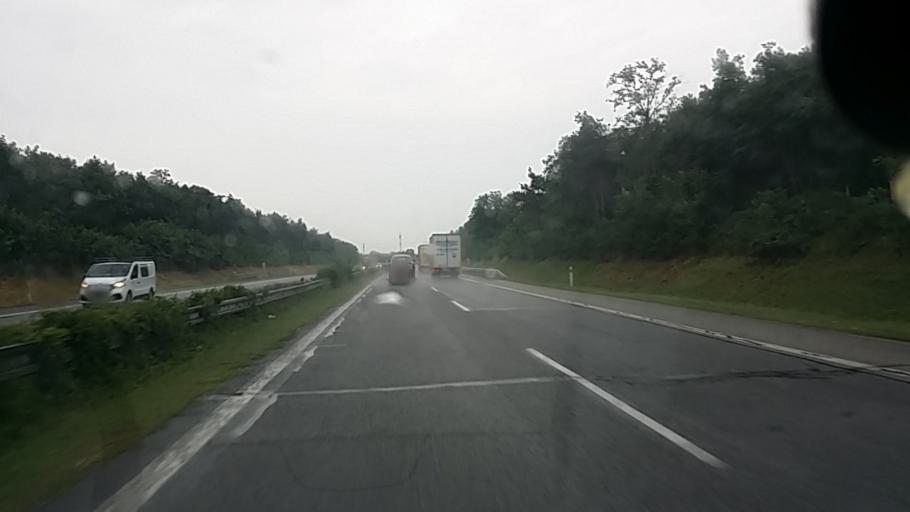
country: SK
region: Bratislavsky
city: Stupava
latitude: 48.3382
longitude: 17.0237
